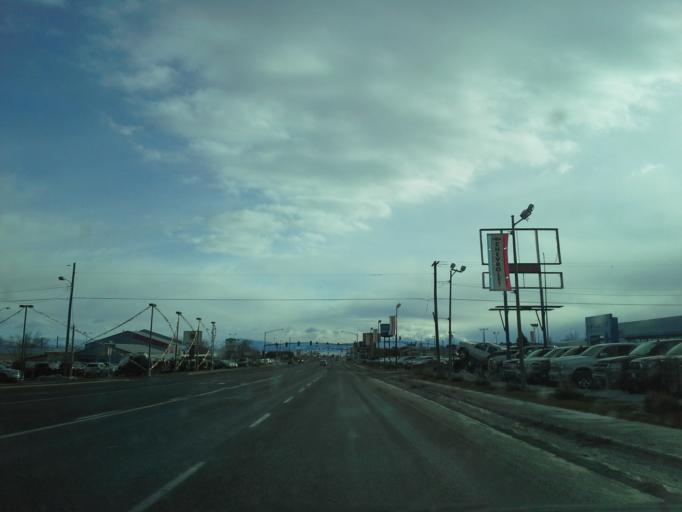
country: US
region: Montana
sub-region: Lewis and Clark County
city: Helena
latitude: 46.6067
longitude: -112.0161
